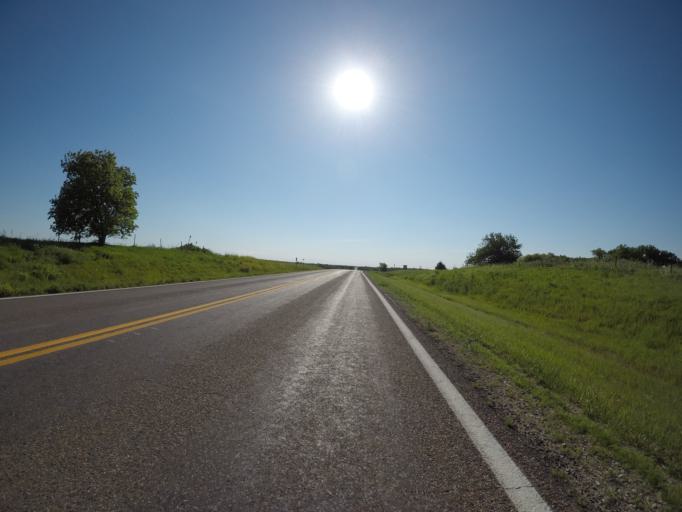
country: US
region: Kansas
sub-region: Lyon County
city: Emporia
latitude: 38.6587
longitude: -96.1891
